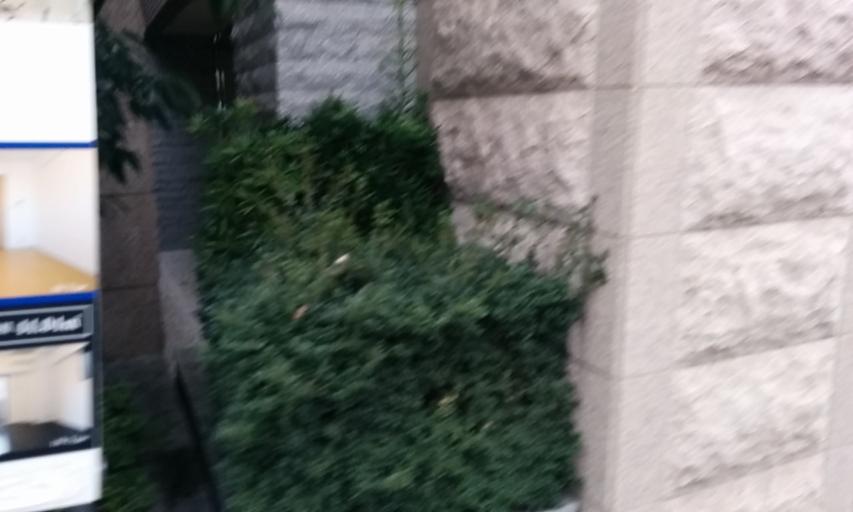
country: JP
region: Tokyo
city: Tokyo
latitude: 35.7039
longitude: 139.7268
